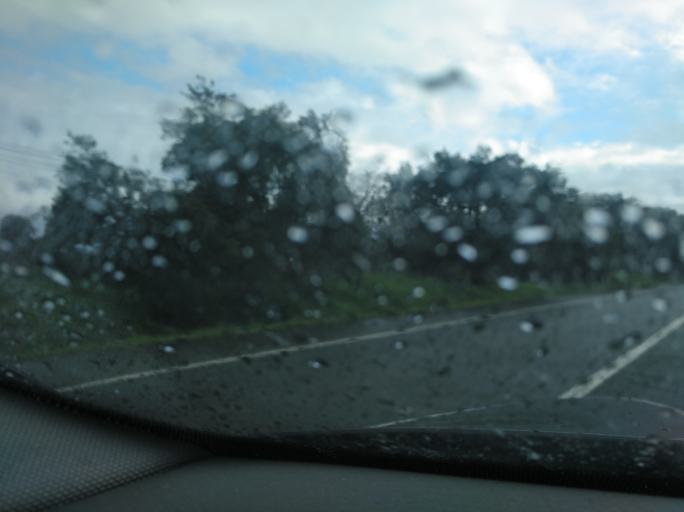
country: PT
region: Setubal
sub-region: Grandola
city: Grandola
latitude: 38.0782
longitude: -8.4168
